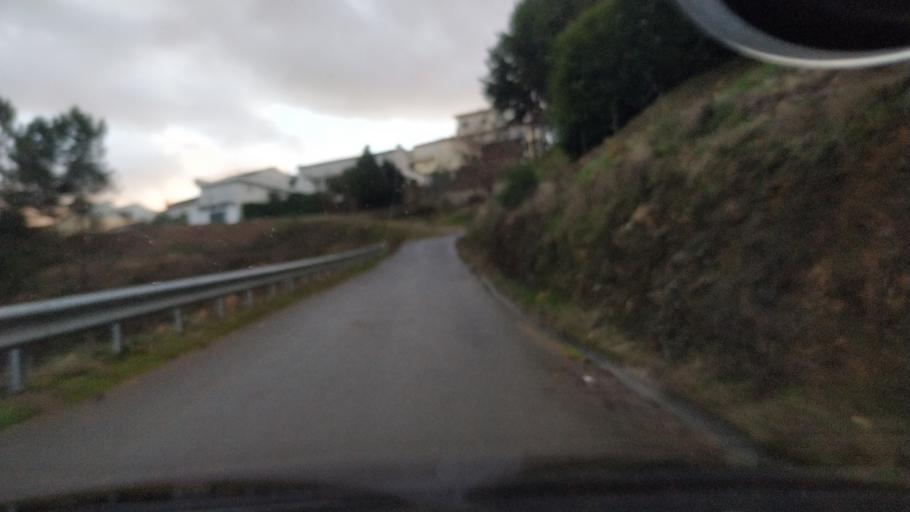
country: PT
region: Vila Real
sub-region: Santa Marta de Penaguiao
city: Santa Marta de Penaguiao
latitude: 41.2513
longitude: -7.7650
